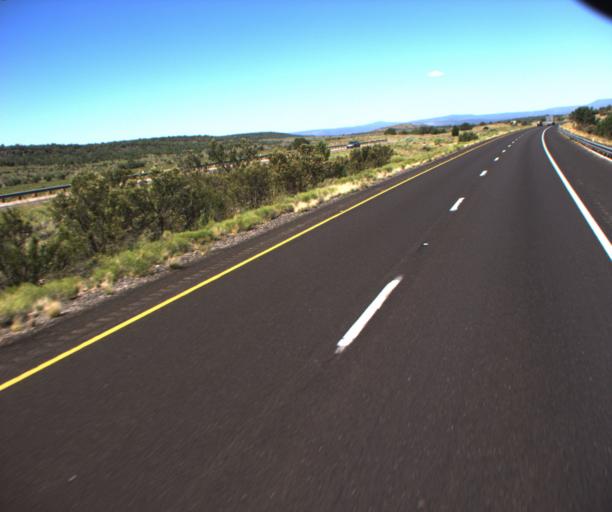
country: US
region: Arizona
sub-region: Yavapai County
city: Paulden
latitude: 35.2728
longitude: -112.7522
